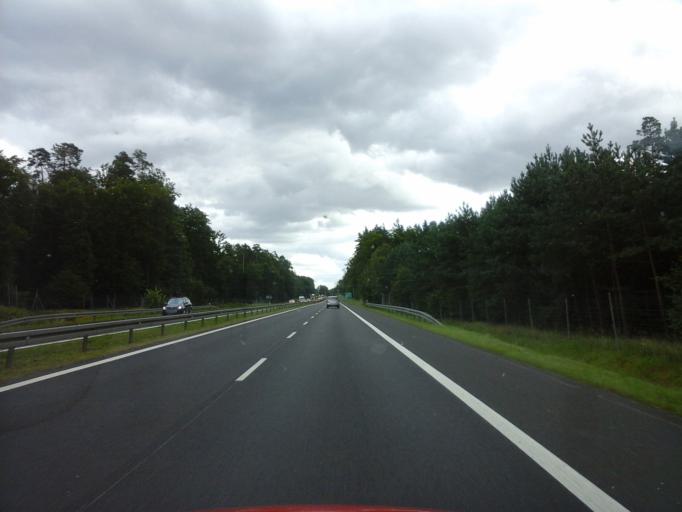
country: PL
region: West Pomeranian Voivodeship
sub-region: Powiat stargardzki
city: Kobylanka
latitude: 53.3513
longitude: 14.8213
